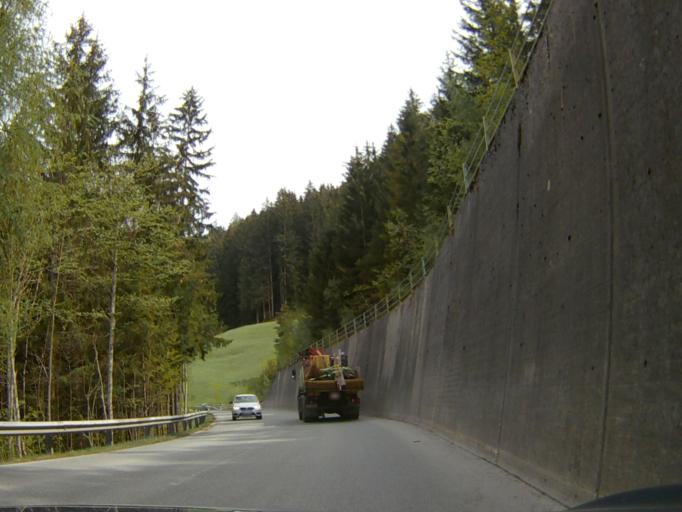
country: AT
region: Tyrol
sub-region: Politischer Bezirk Schwaz
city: Hainzenberg
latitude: 47.2155
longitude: 11.9074
